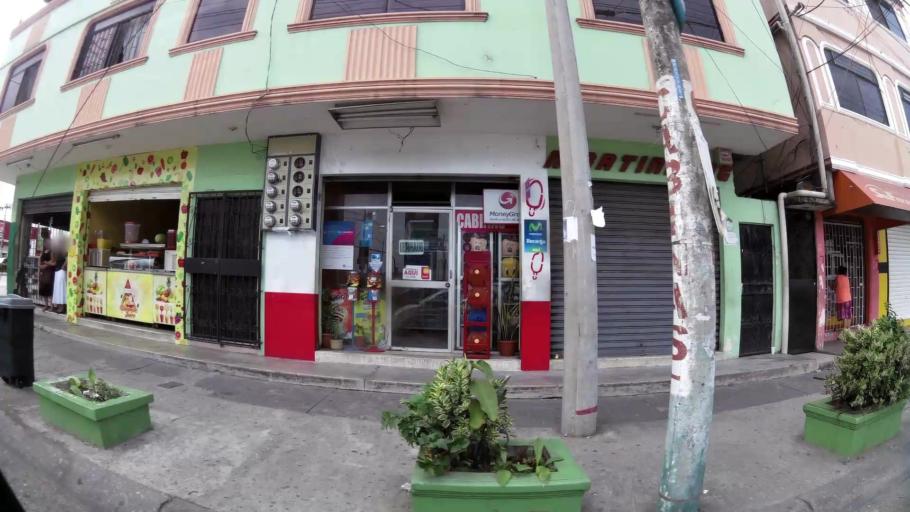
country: EC
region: Guayas
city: Eloy Alfaro
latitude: -2.1209
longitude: -79.8999
